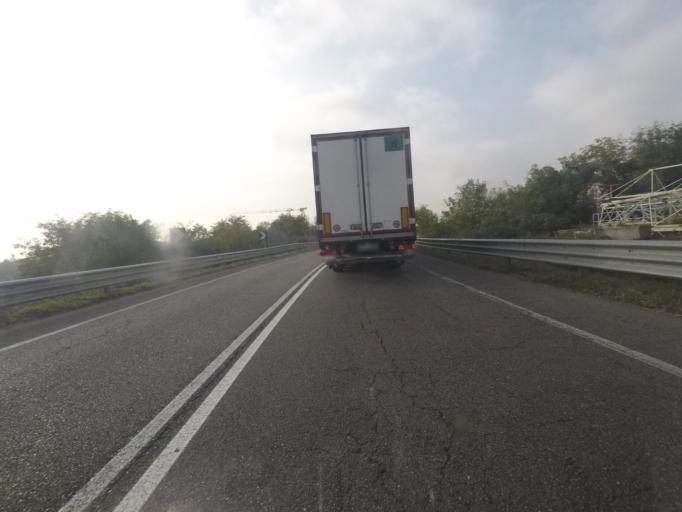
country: IT
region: Lombardy
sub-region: Provincia di Monza e Brianza
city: Burago di Molgora
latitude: 45.6117
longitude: 9.3872
